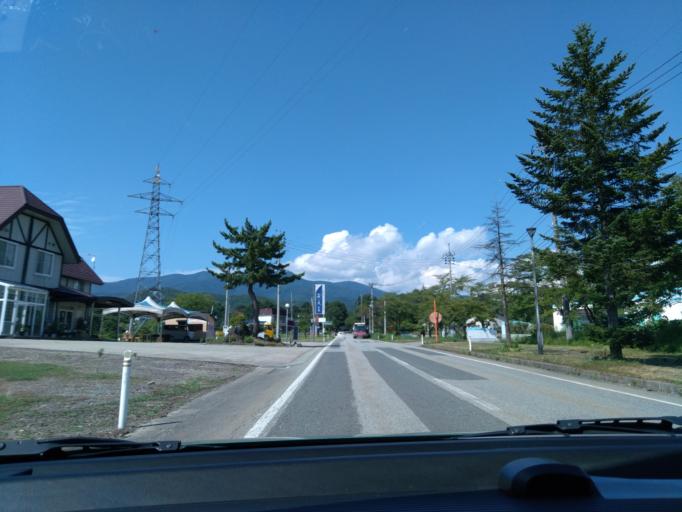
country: JP
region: Akita
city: Kakunodatemachi
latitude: 39.7438
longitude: 140.7201
